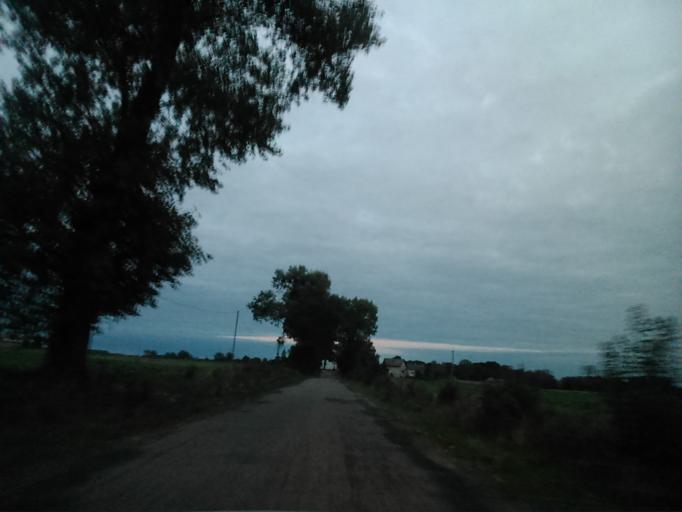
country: PL
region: Kujawsko-Pomorskie
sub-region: Powiat golubsko-dobrzynski
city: Kowalewo Pomorskie
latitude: 53.1253
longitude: 18.9224
